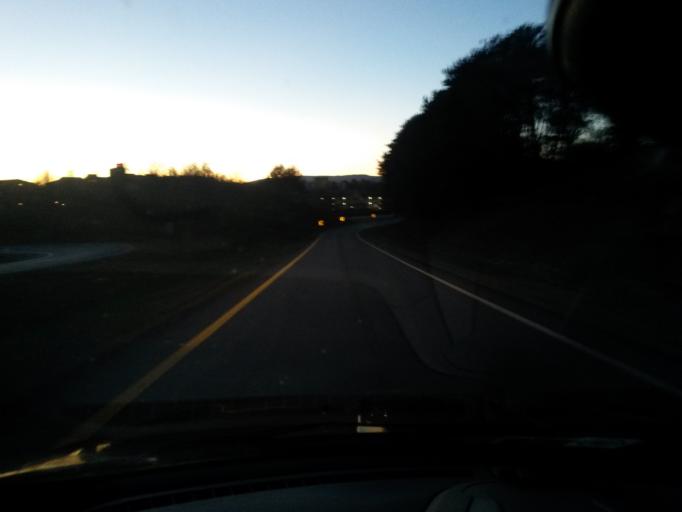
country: US
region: Virginia
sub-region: Roanoke County
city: Hollins
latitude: 37.3105
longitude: -79.9737
